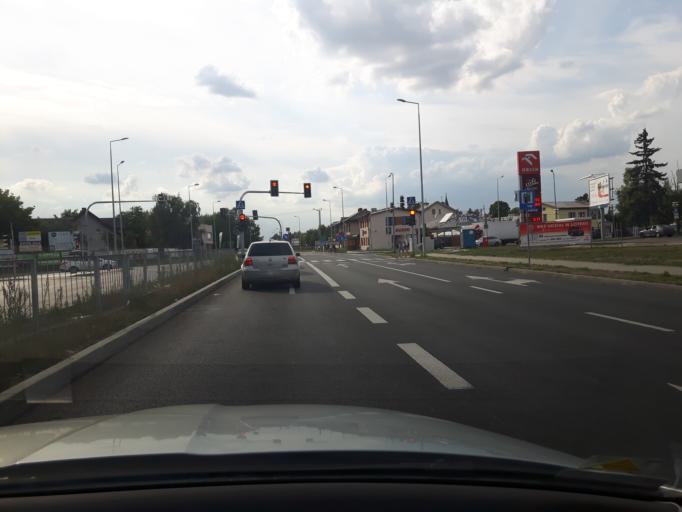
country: PL
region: Masovian Voivodeship
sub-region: Powiat piaseczynski
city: Piaseczno
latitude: 52.0816
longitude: 21.0160
